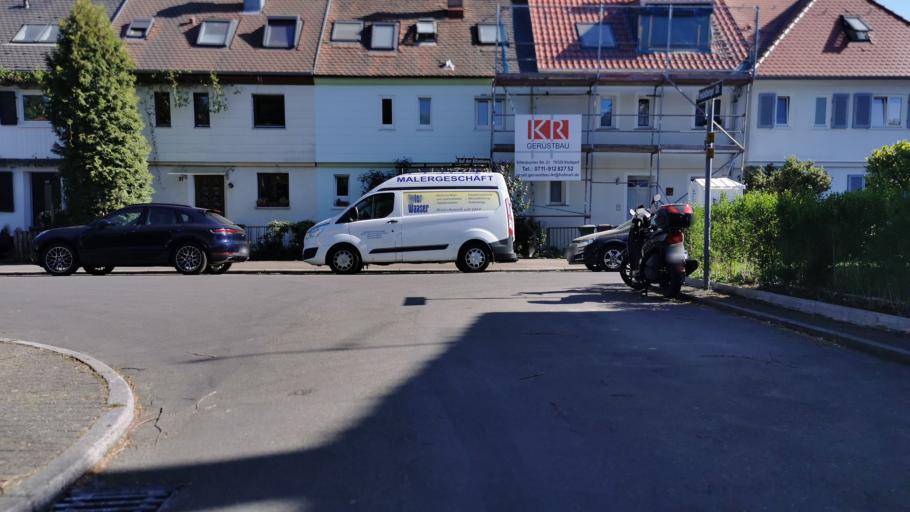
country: DE
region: Baden-Wuerttemberg
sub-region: Regierungsbezirk Stuttgart
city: Stuttgart-Ost
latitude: 48.8106
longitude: 9.2063
